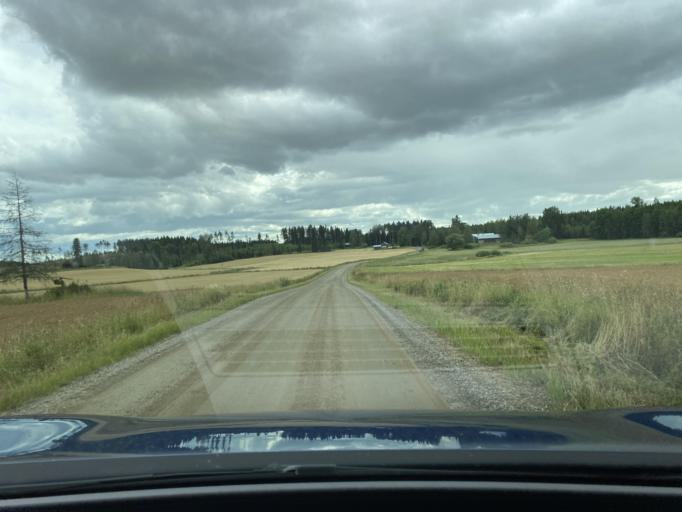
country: FI
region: Pirkanmaa
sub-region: Lounais-Pirkanmaa
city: Punkalaidun
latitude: 61.1840
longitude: 23.1852
